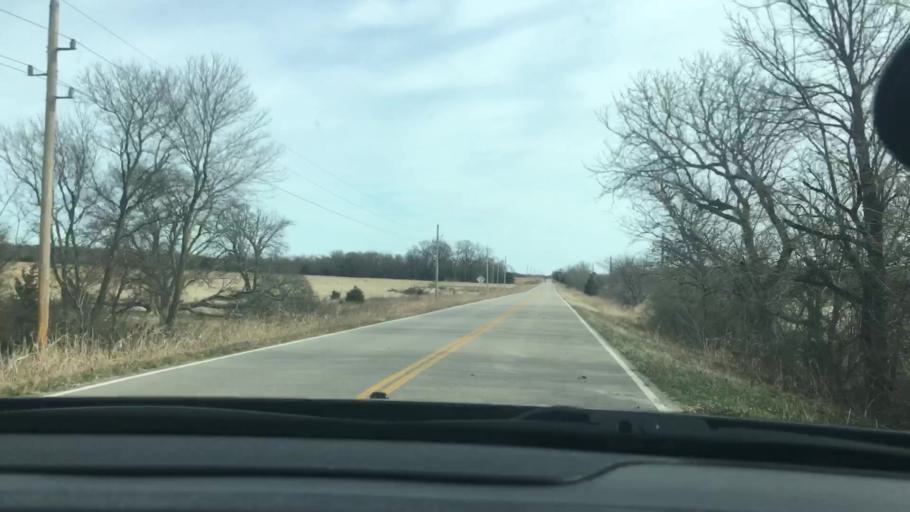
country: US
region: Oklahoma
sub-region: Murray County
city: Sulphur
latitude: 34.4048
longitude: -96.8621
